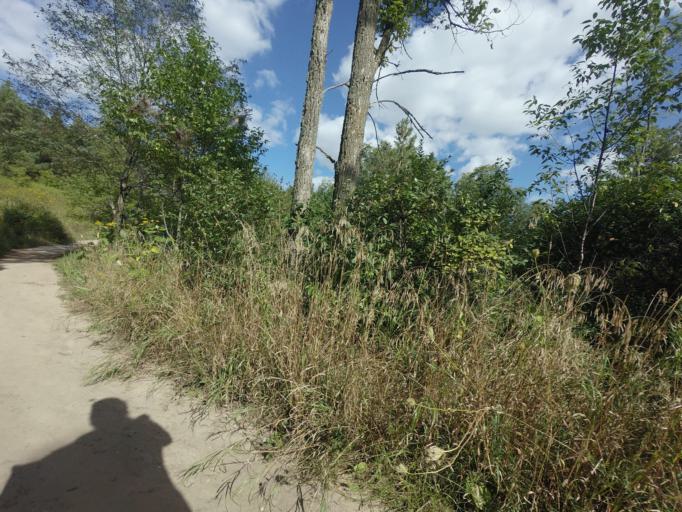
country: CA
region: Ontario
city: Orangeville
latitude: 43.8221
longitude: -80.0118
